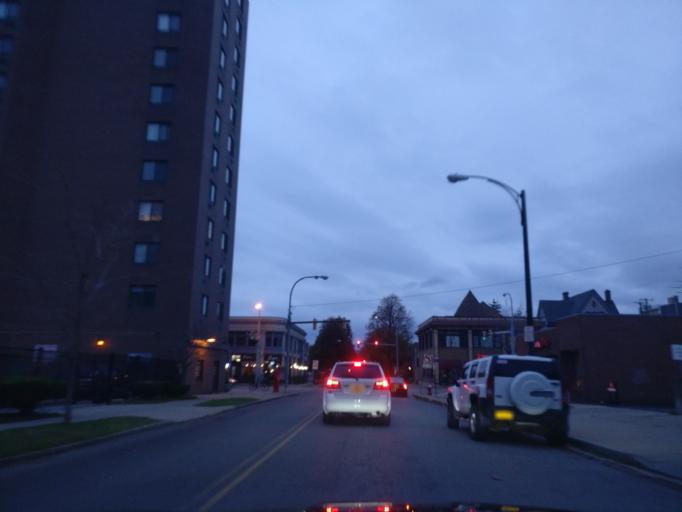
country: US
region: New York
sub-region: Erie County
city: Buffalo
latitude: 42.9113
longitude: -78.8763
